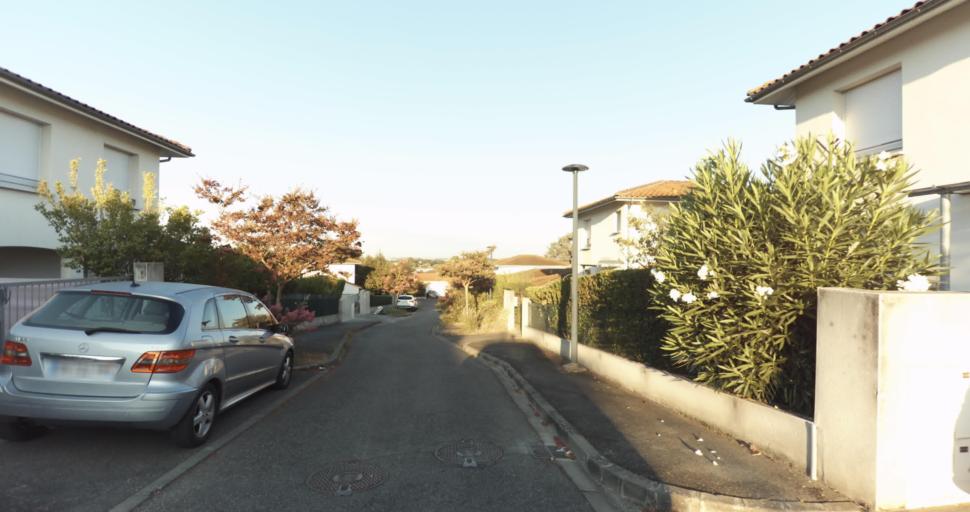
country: FR
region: Midi-Pyrenees
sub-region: Departement de la Haute-Garonne
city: L'Union
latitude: 43.6561
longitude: 1.4756
